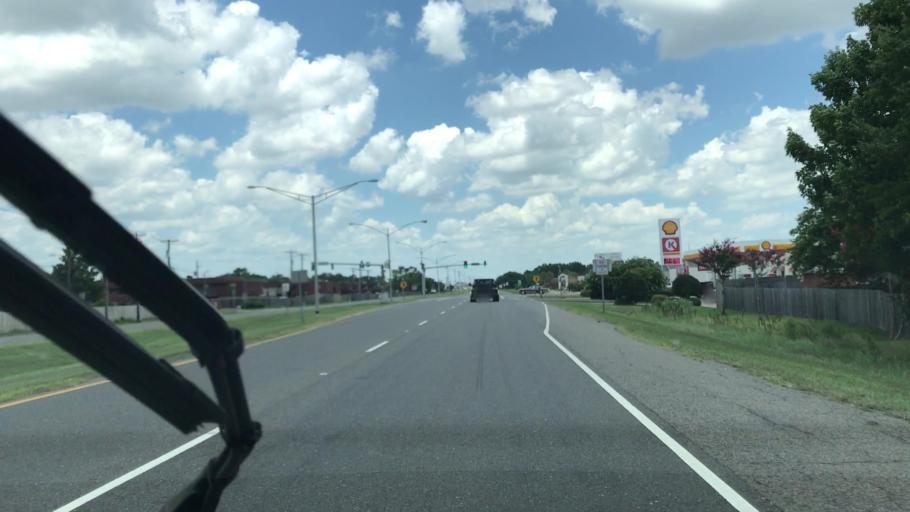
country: US
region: Louisiana
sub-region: Bossier Parish
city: Bossier City
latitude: 32.4118
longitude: -93.7001
